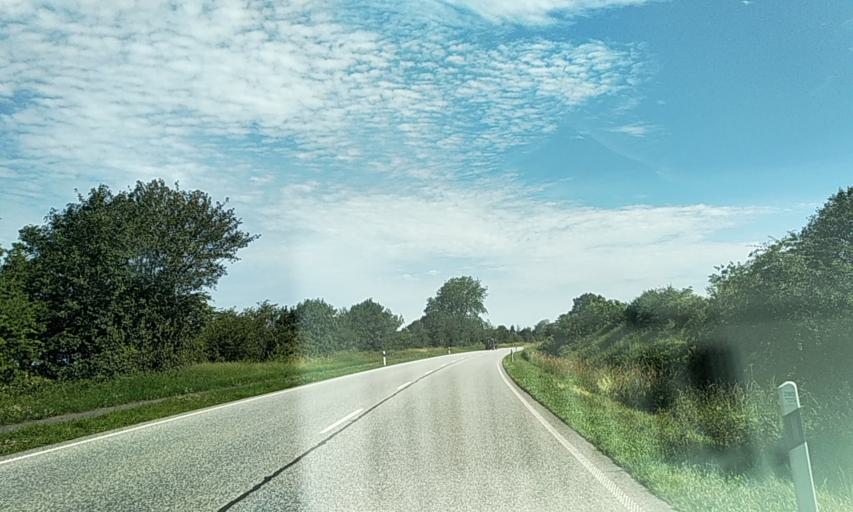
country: DE
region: Schleswig-Holstein
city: Jagel
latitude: 54.4393
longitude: 9.5340
